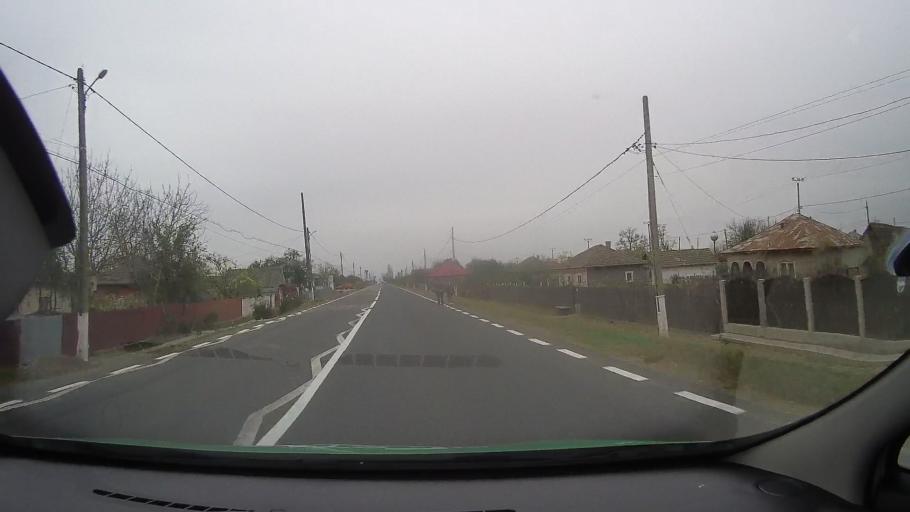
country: RO
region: Ialomita
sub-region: Comuna Giurgeni
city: Giurgeni
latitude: 44.7416
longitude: 27.8561
